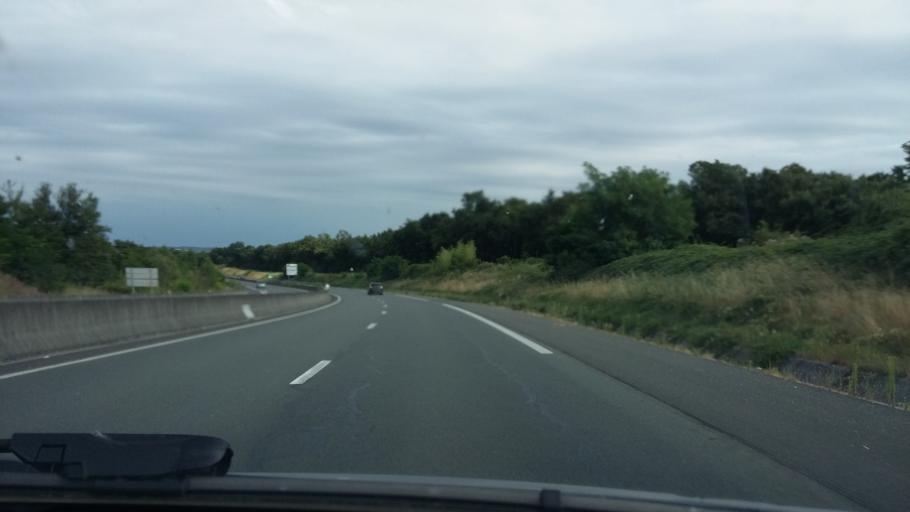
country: FR
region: Poitou-Charentes
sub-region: Departement de la Charente
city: Saint-Yrieix-sur-Charente
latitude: 45.6843
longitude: 0.1159
